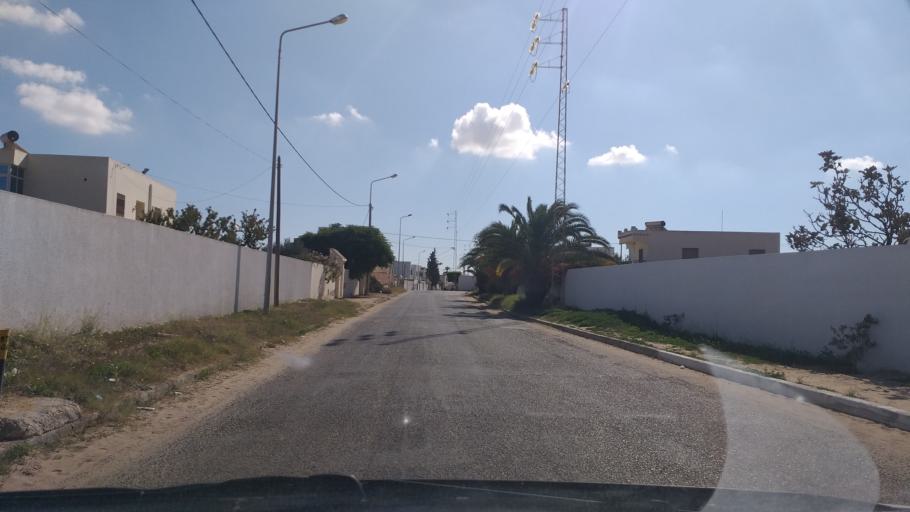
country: TN
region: Safaqis
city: Al Qarmadah
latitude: 34.8022
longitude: 10.7717
